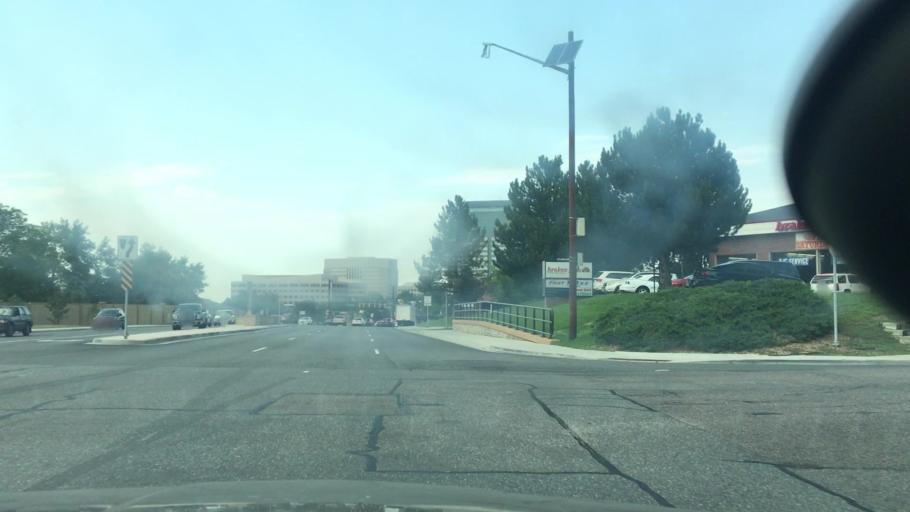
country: US
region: Colorado
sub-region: Arapahoe County
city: Castlewood
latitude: 39.5929
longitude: -104.8882
